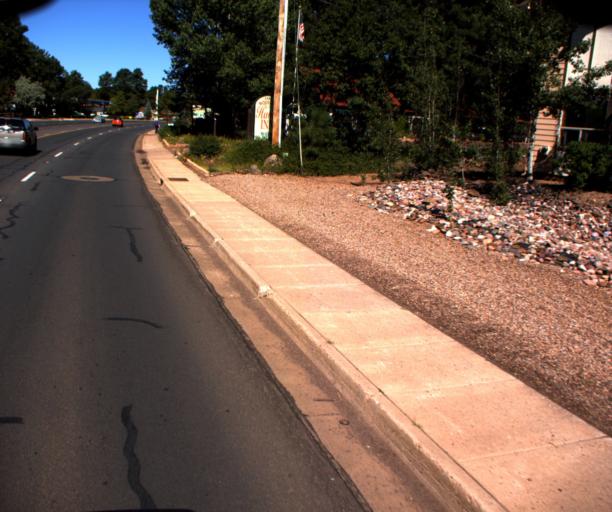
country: US
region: Arizona
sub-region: Navajo County
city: Pinetop-Lakeside
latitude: 34.1261
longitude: -109.9413
